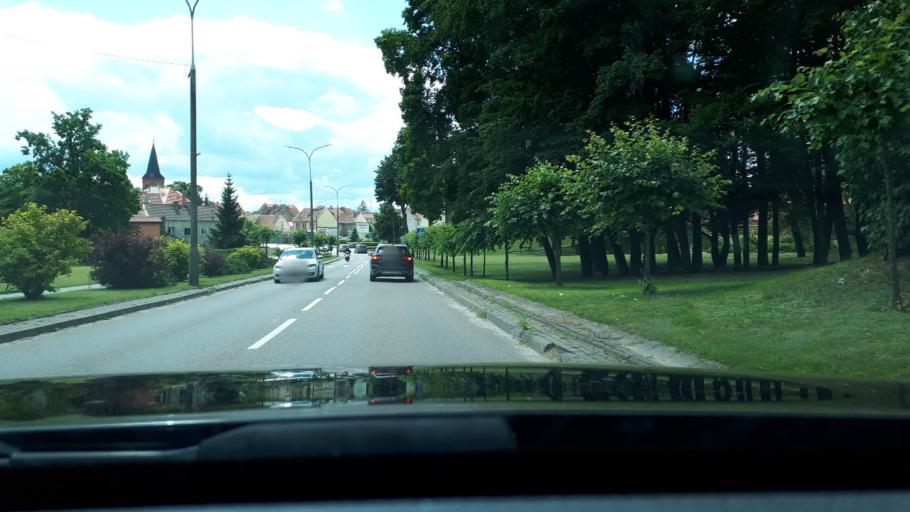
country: PL
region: Warmian-Masurian Voivodeship
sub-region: Powiat olsztynski
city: Olsztynek
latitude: 53.5852
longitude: 20.2844
